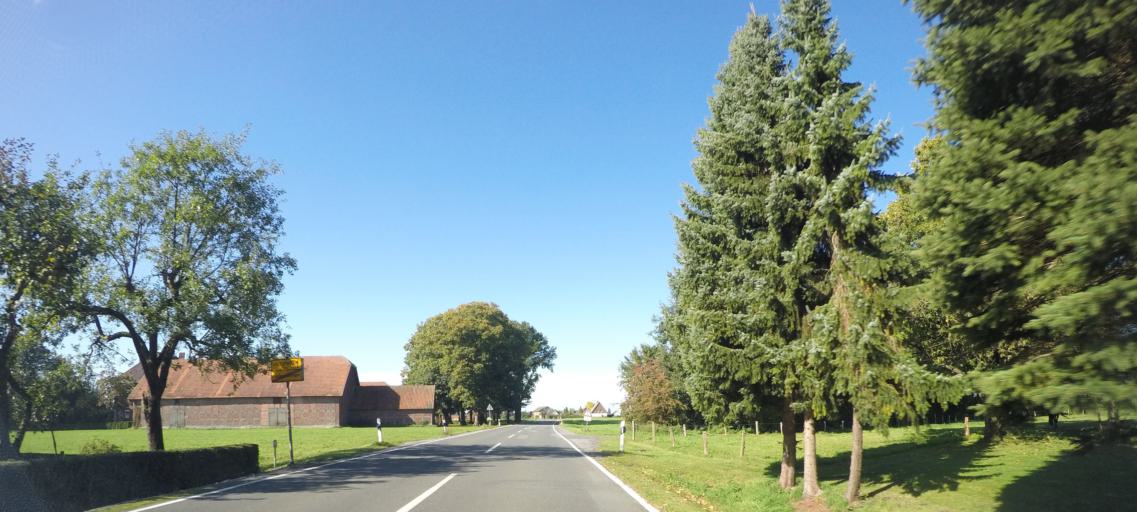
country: DE
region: North Rhine-Westphalia
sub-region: Regierungsbezirk Munster
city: Wadersloh
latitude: 51.6647
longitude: 8.2290
